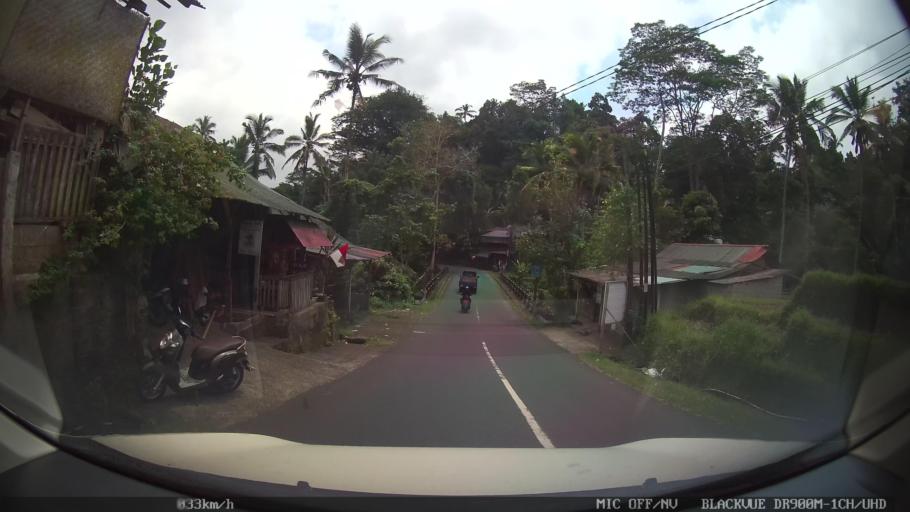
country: ID
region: Bali
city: Banjar Brahmanabukit
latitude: -8.4465
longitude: 115.3741
